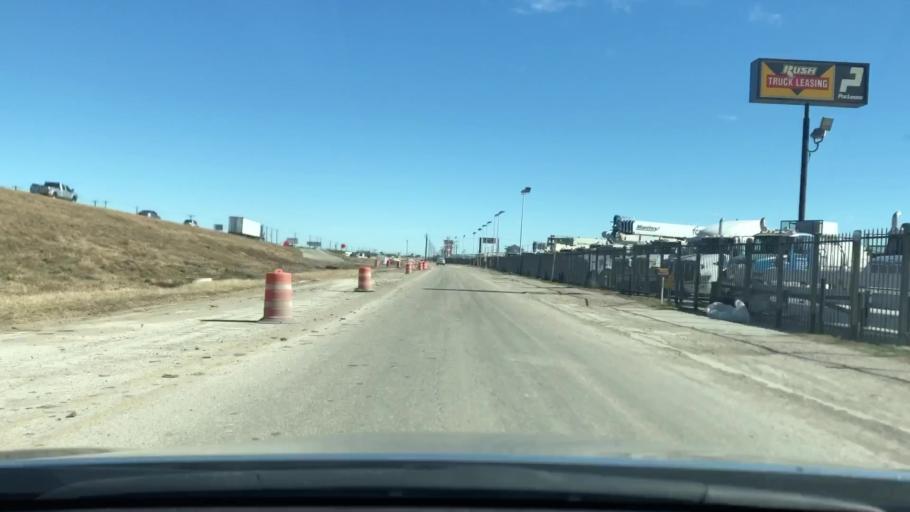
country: US
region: Texas
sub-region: Bexar County
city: Converse
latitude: 29.4586
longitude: -98.3160
